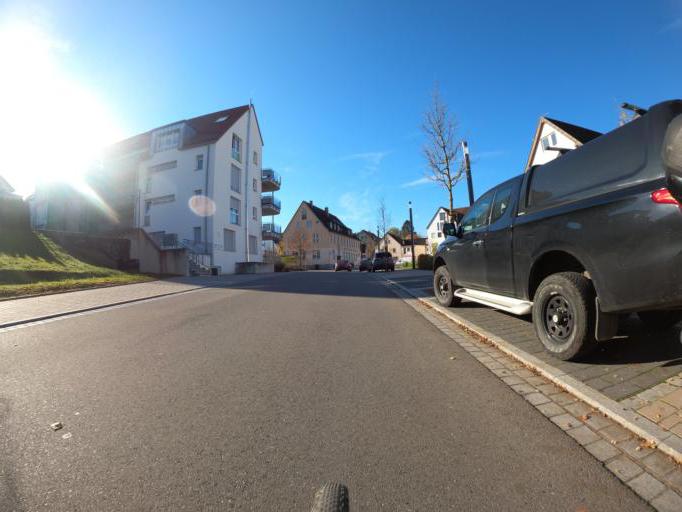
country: DE
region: Baden-Wuerttemberg
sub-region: Regierungsbezirk Stuttgart
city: Magstadt
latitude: 48.7407
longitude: 8.9633
